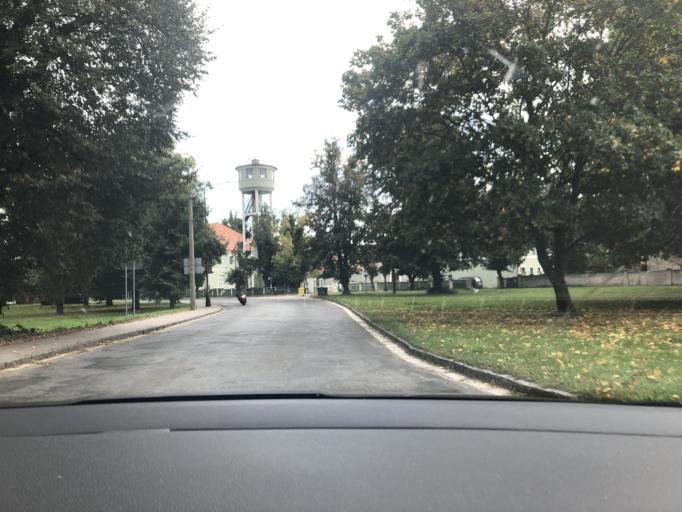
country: CZ
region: Pardubicky
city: Recany nad Labem
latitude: 50.0594
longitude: 15.4840
